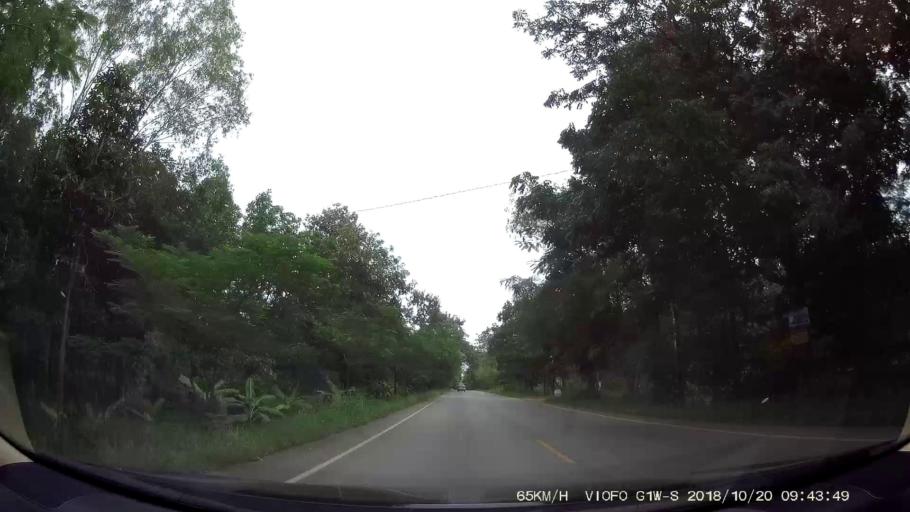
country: TH
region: Chaiyaphum
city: Khon San
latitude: 16.4771
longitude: 101.9465
